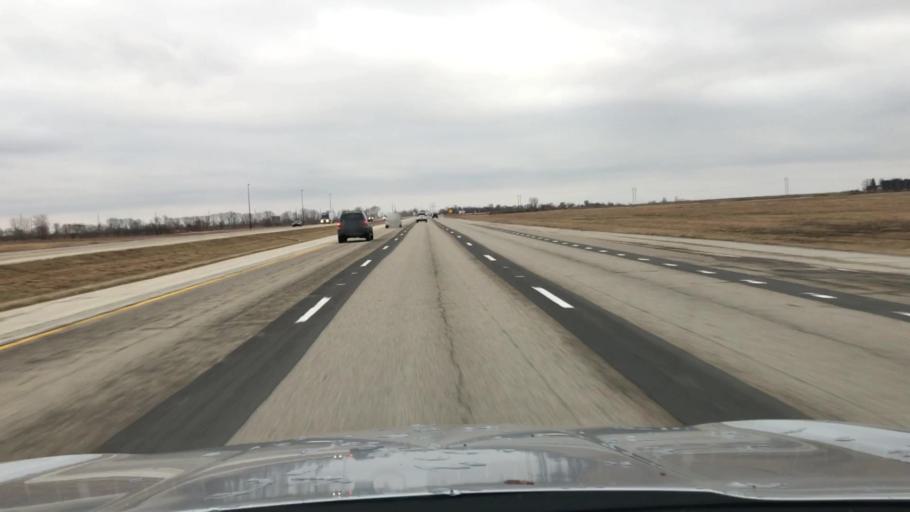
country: US
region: Illinois
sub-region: Logan County
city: Lincoln
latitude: 40.1115
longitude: -89.4166
